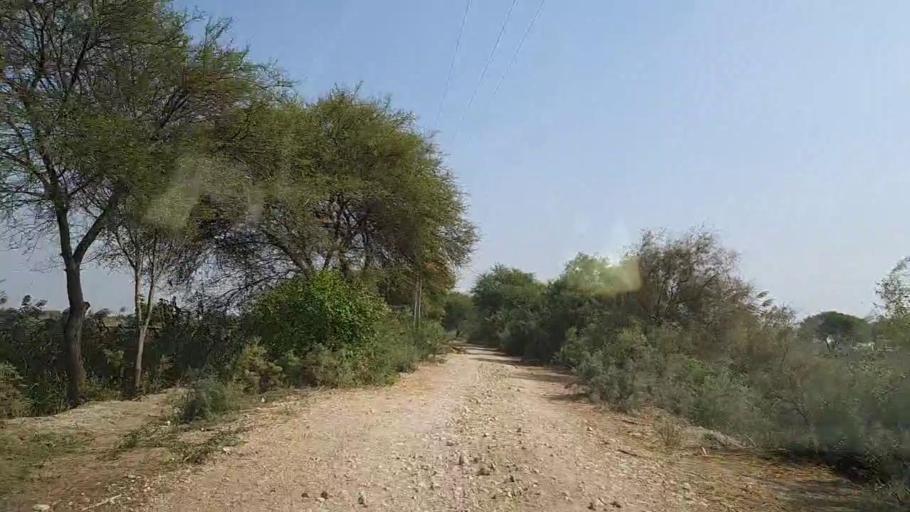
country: PK
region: Sindh
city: Mirpur Sakro
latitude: 24.5288
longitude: 67.7981
